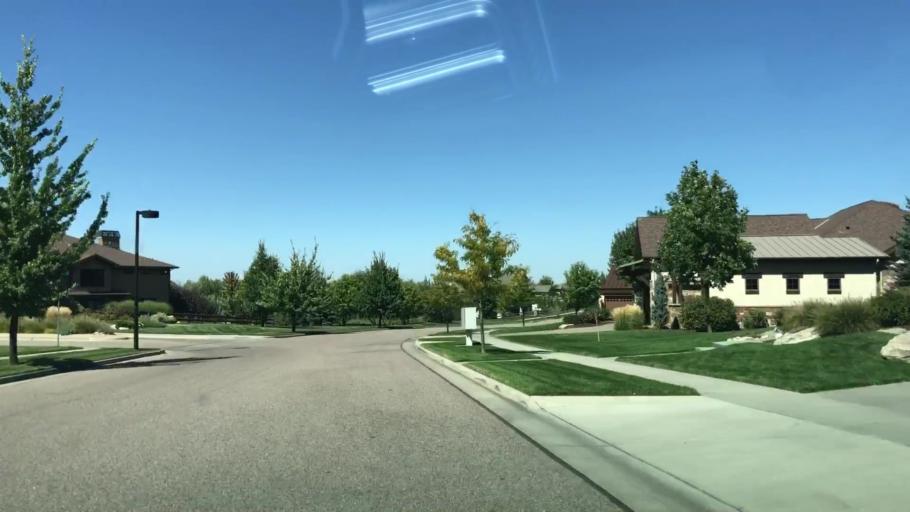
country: US
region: Colorado
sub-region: Weld County
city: Windsor
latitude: 40.5323
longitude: -104.9574
